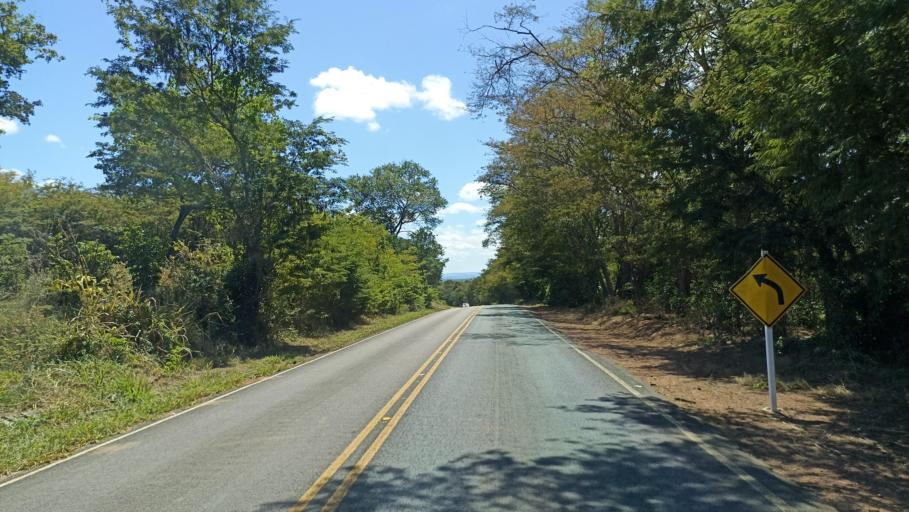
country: BR
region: Bahia
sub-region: Andarai
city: Vera Cruz
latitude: -12.7865
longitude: -41.3286
